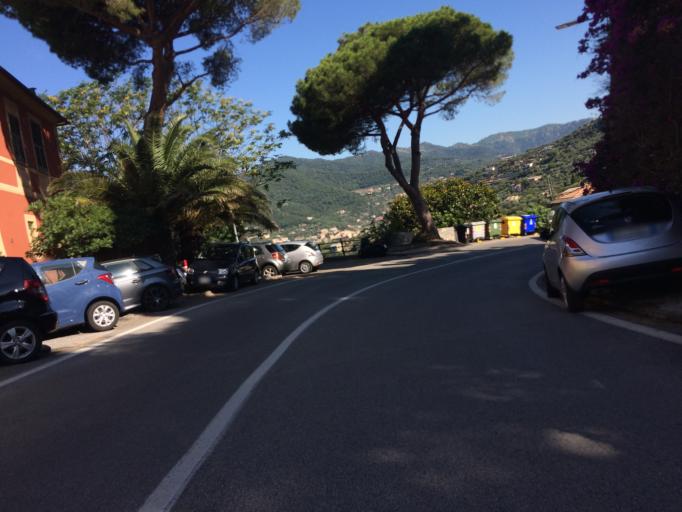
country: IT
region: Liguria
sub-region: Provincia di Genova
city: Camogli
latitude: 44.3544
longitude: 9.1542
